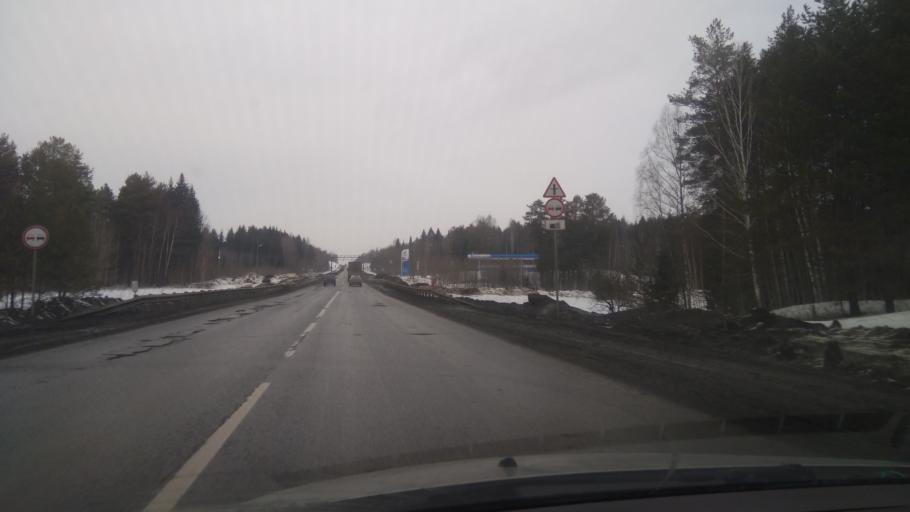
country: RU
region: Perm
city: Kungur
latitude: 57.3084
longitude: 56.9773
